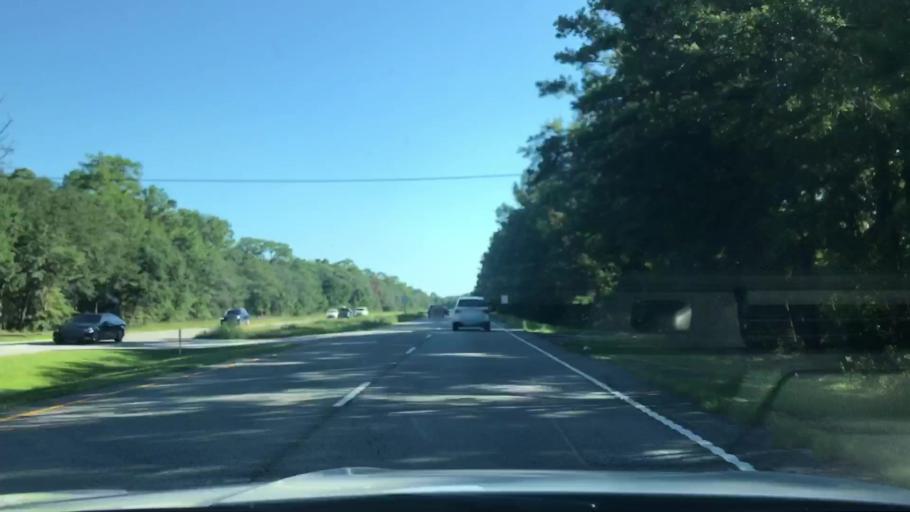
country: US
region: South Carolina
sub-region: Georgetown County
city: Georgetown
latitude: 33.3775
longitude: -79.2119
